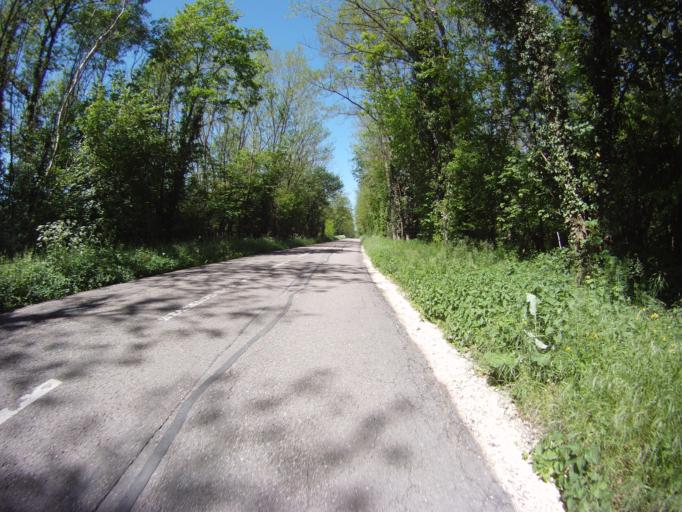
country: FR
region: Lorraine
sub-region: Departement de Meurthe-et-Moselle
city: Dommartin-les-Toul
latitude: 48.6471
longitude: 5.9173
